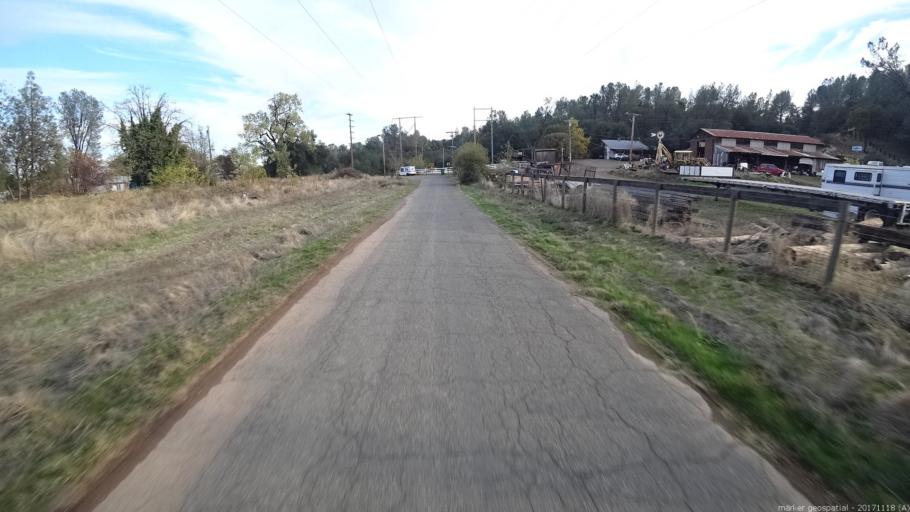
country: US
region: California
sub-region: Shasta County
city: Anderson
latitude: 40.4573
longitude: -122.3398
